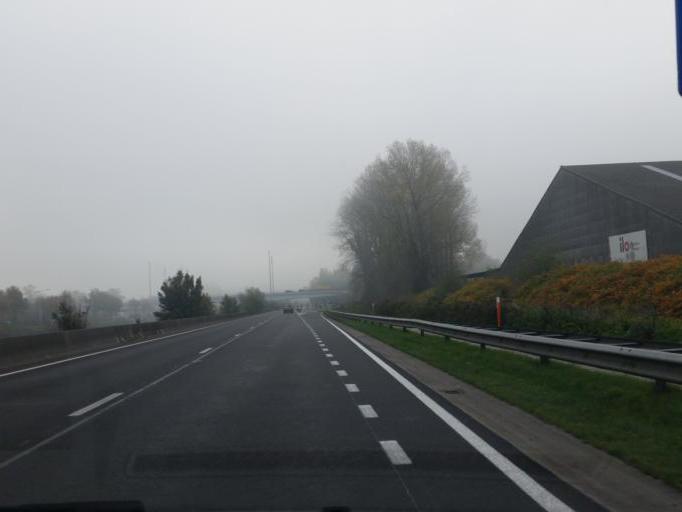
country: BE
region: Flanders
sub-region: Provincie Oost-Vlaanderen
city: Gent
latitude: 51.0553
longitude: 3.6683
